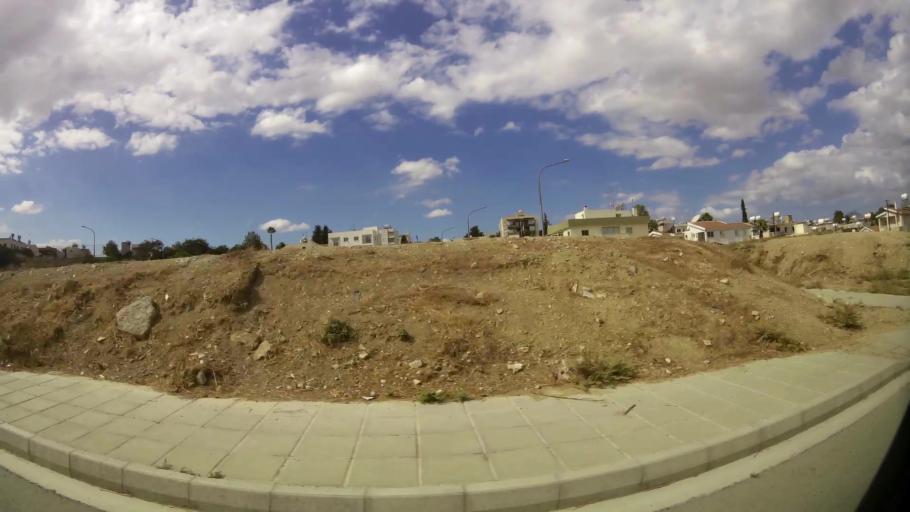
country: CY
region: Lefkosia
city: Nicosia
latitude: 35.1751
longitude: 33.3889
